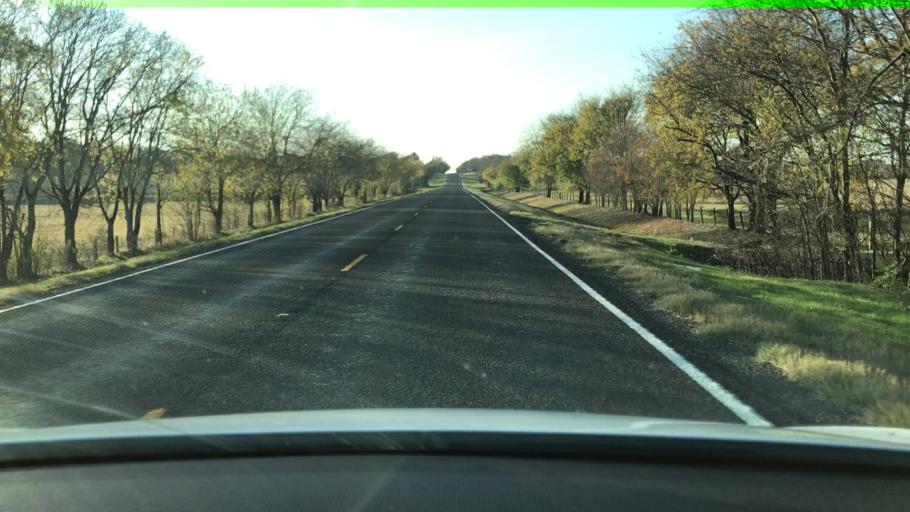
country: US
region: Texas
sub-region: Kaufman County
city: Kemp
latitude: 32.5701
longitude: -96.1414
